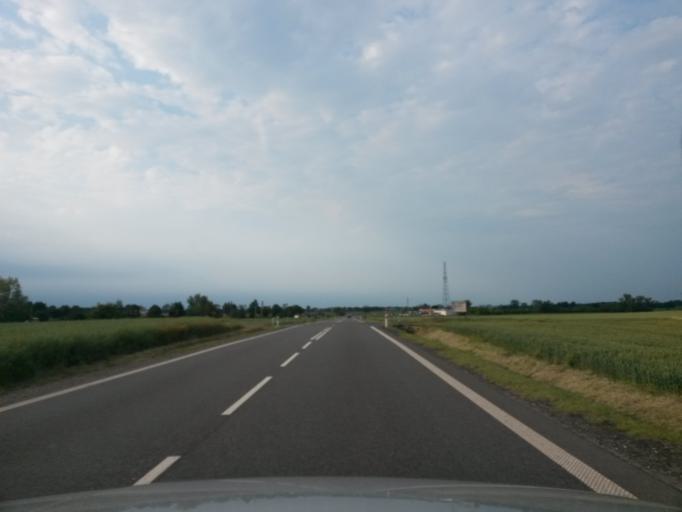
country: PL
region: Lower Silesian Voivodeship
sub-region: Powiat sredzki
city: Ciechow
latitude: 51.0319
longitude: 16.5811
